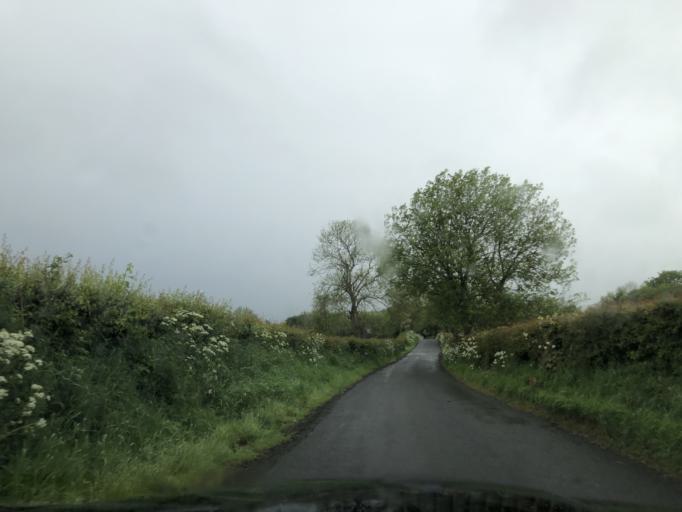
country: GB
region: Northern Ireland
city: Dunloy
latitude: 55.1381
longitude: -6.3752
